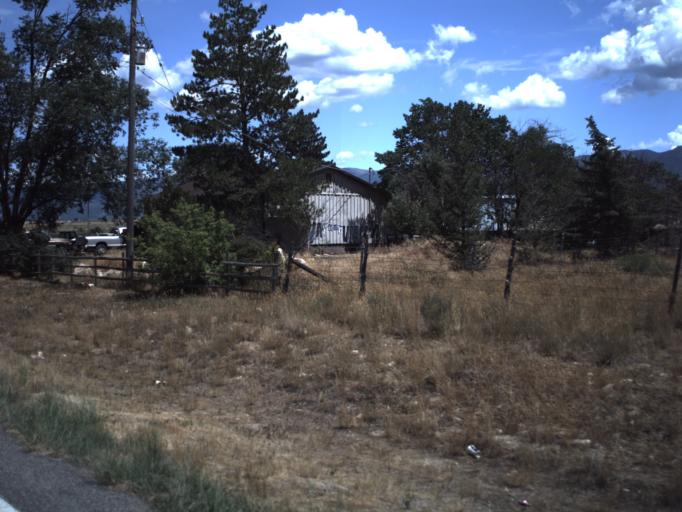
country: US
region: Utah
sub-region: Sanpete County
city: Mount Pleasant
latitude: 39.4979
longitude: -111.4908
